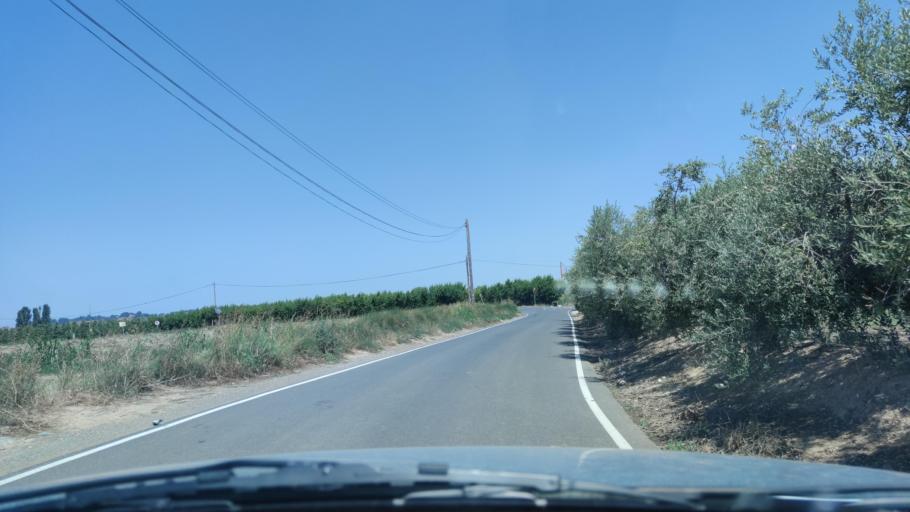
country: ES
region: Catalonia
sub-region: Provincia de Lleida
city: Alpicat
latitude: 41.6571
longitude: 0.5709
